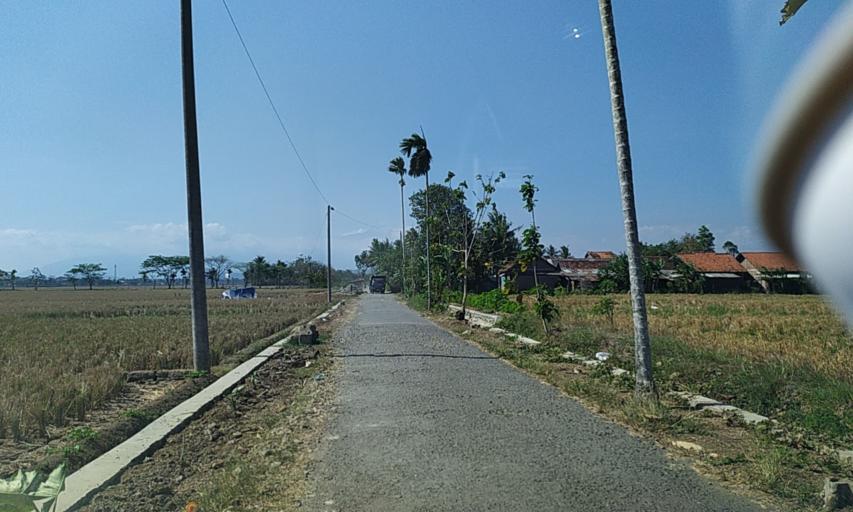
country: ID
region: Central Java
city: Glempang Tengah
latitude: -7.5930
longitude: 109.1726
